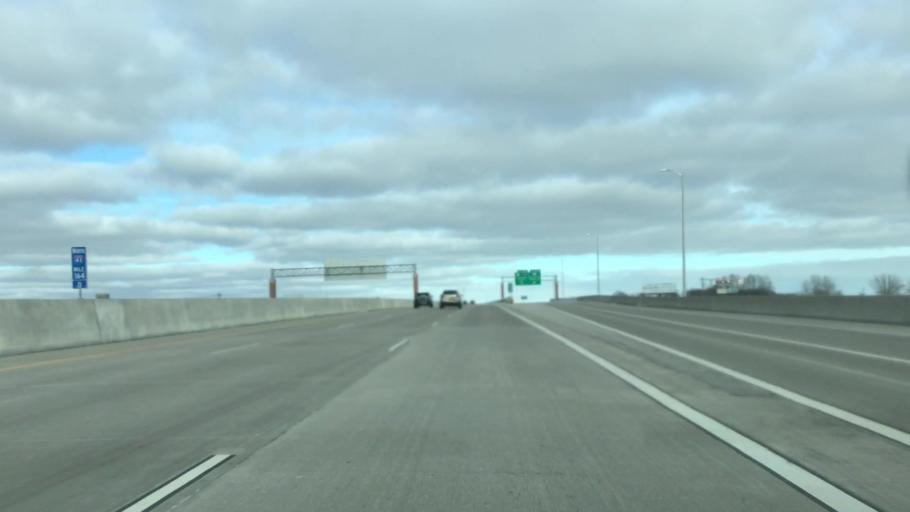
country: US
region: Wisconsin
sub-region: Brown County
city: Ashwaubenon
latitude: 44.4635
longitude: -88.0822
